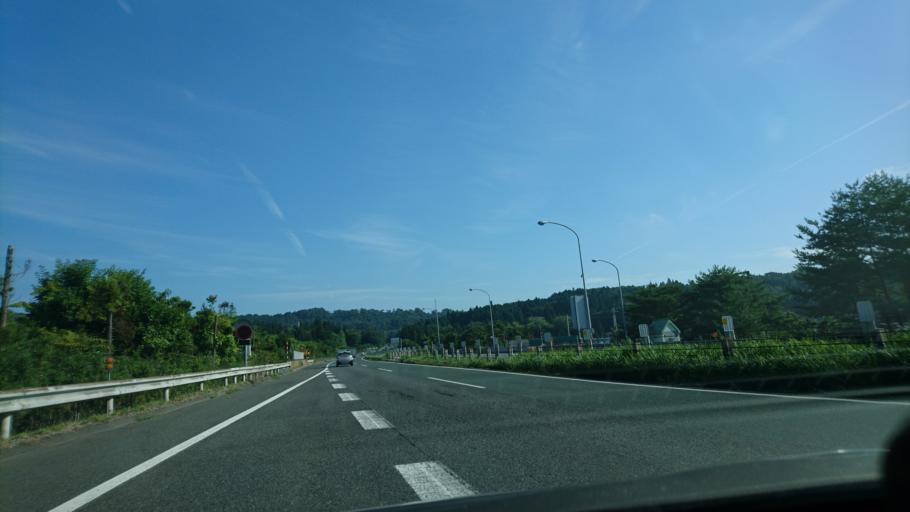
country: JP
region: Iwate
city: Ichinoseki
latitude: 38.9384
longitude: 141.1014
